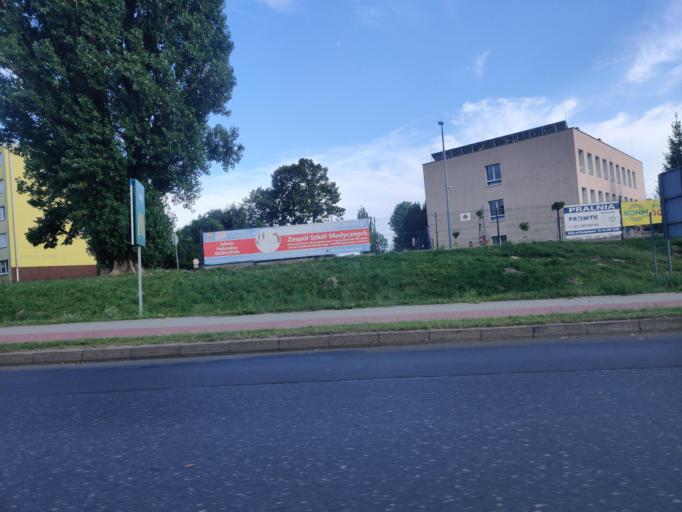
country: PL
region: Greater Poland Voivodeship
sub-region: Konin
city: Konin
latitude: 52.2268
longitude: 18.2602
